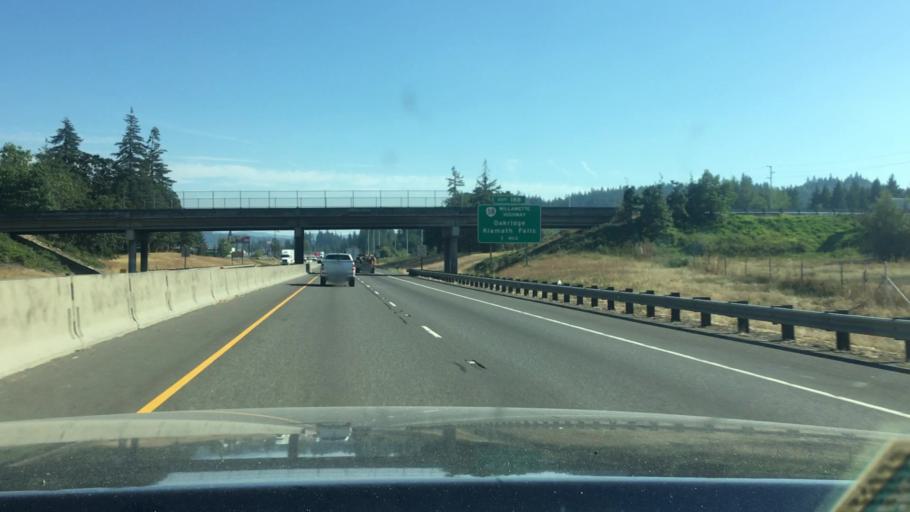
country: US
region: Oregon
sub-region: Lane County
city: Springfield
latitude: 44.0145
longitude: -123.0239
